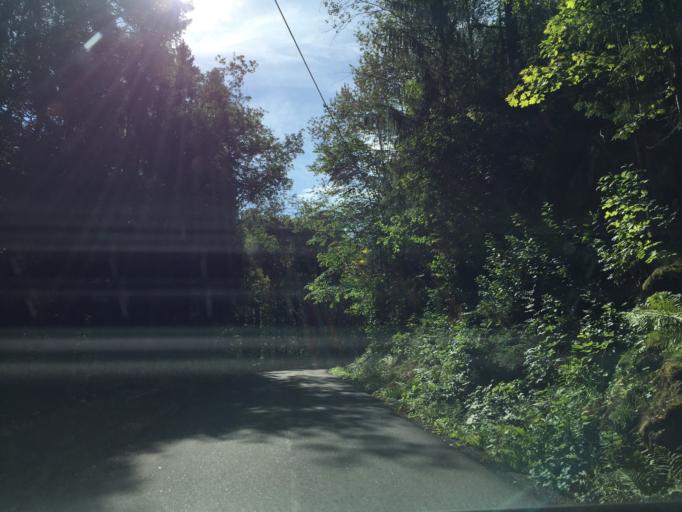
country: NO
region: Vestfold
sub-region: Hof
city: Hof
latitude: 59.4830
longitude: 10.1499
